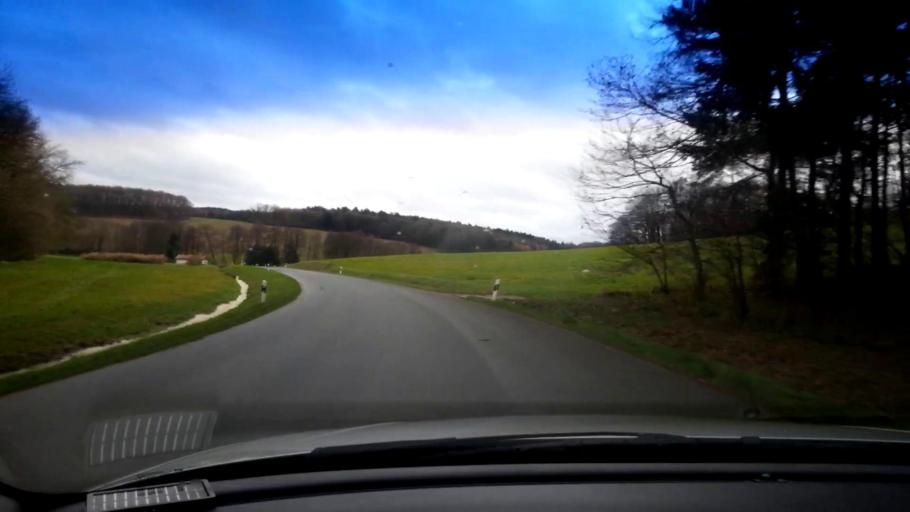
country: DE
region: Bavaria
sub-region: Upper Franconia
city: Zapfendorf
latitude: 50.0191
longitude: 10.9637
